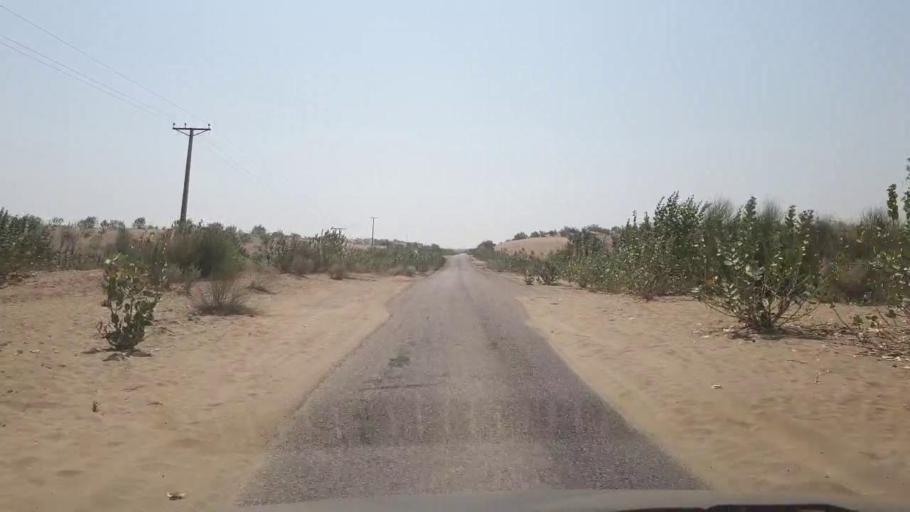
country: PK
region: Sindh
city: Chor
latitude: 25.6591
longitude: 70.1671
